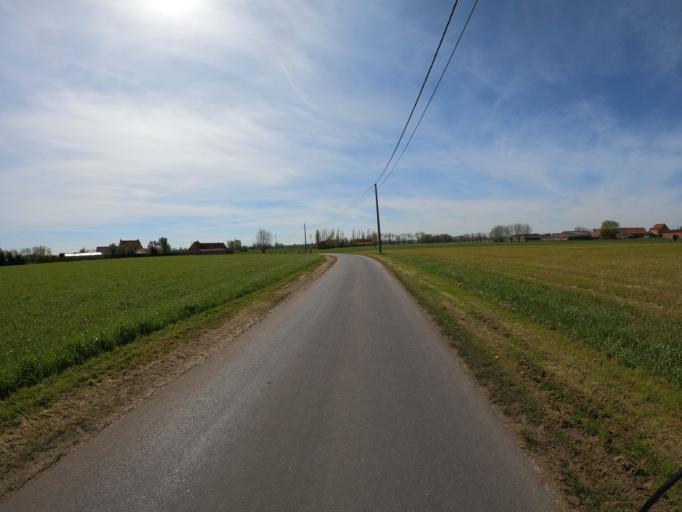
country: BE
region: Flanders
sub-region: Provincie West-Vlaanderen
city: Ruiselede
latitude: 51.0273
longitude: 3.3659
